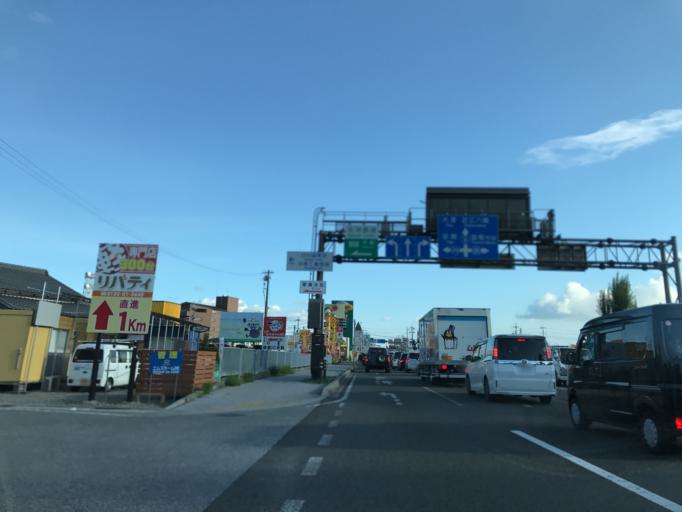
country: JP
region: Shiga Prefecture
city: Hikone
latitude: 35.2682
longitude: 136.2666
